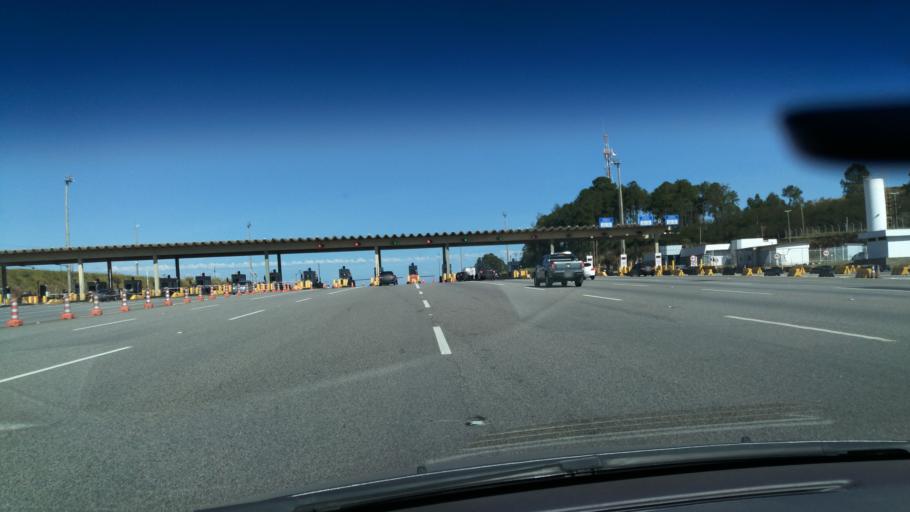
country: BR
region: Sao Paulo
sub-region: Jaguariuna
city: Jaguariuna
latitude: -22.7701
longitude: -47.0221
